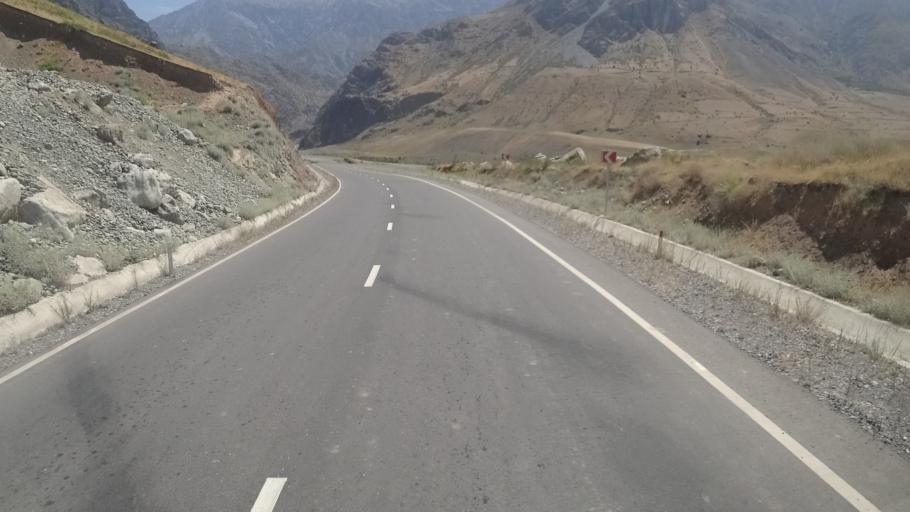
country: AF
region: Badakhshan
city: Deh Khwahan
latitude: 37.9397
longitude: 70.2230
